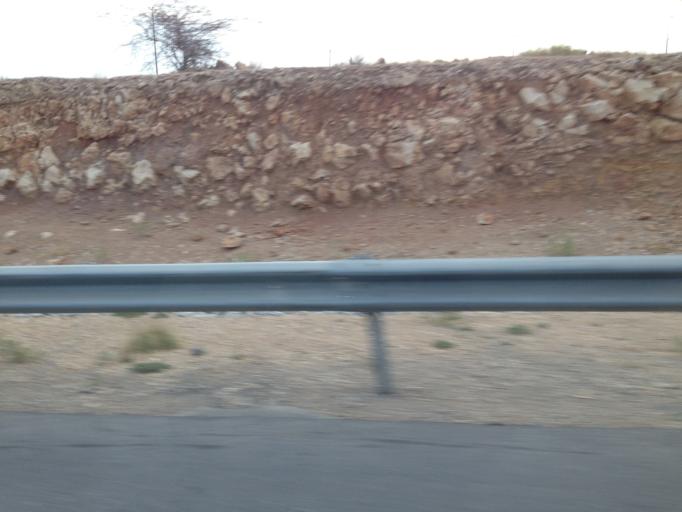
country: OM
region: Muhafazat Masqat
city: Bawshar
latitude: 23.5598
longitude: 58.3374
